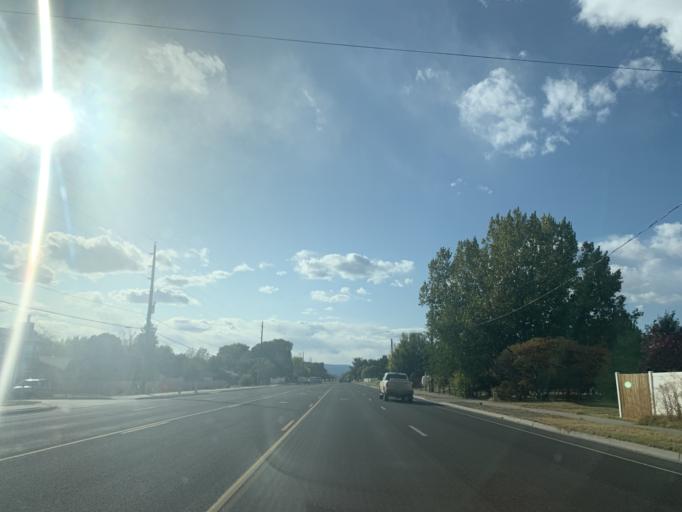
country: US
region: Colorado
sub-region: Mesa County
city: Fruitvale
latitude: 39.0918
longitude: -108.4837
